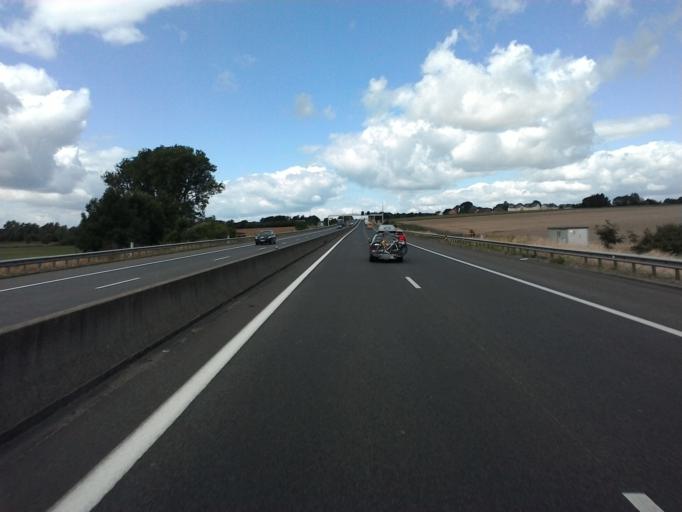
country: LU
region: Luxembourg
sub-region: Canton de Capellen
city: Steinfort
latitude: 49.6362
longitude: 5.9263
